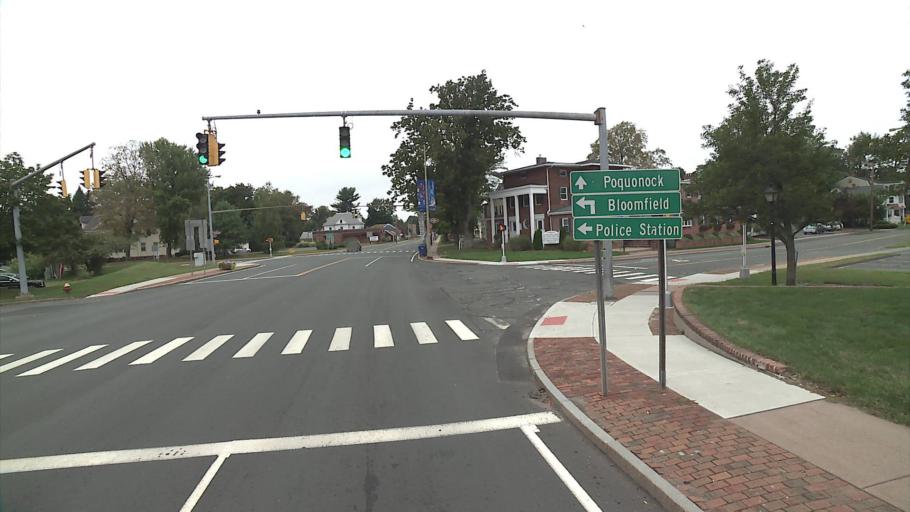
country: US
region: Connecticut
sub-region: Hartford County
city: Windsor
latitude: 41.8530
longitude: -72.6443
